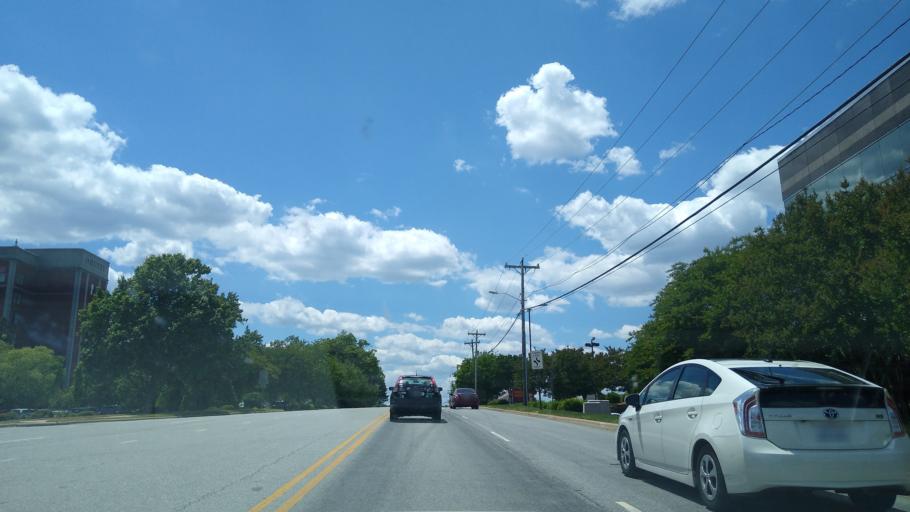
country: US
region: North Carolina
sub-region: Guilford County
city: Greensboro
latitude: 36.0880
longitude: -79.8261
